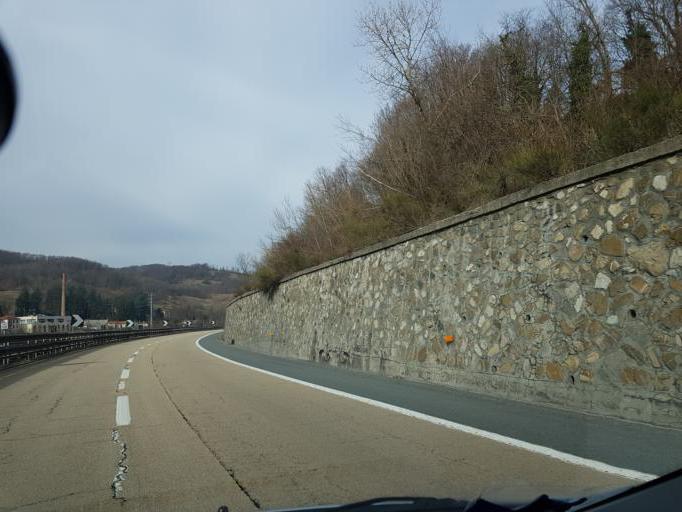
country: IT
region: Liguria
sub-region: Provincia di Genova
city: Busalla
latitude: 44.5770
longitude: 8.9451
